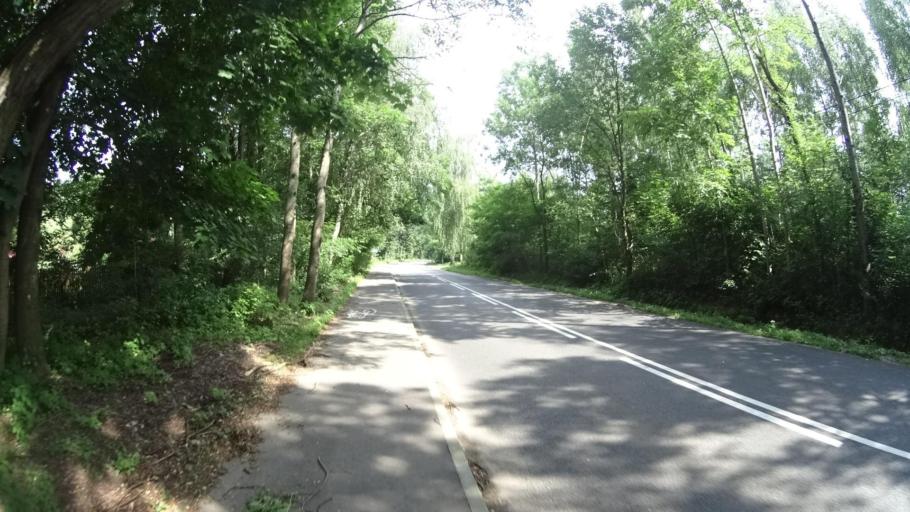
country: PL
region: Masovian Voivodeship
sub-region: Powiat piaseczynski
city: Tarczyn
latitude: 52.0292
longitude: 20.7832
